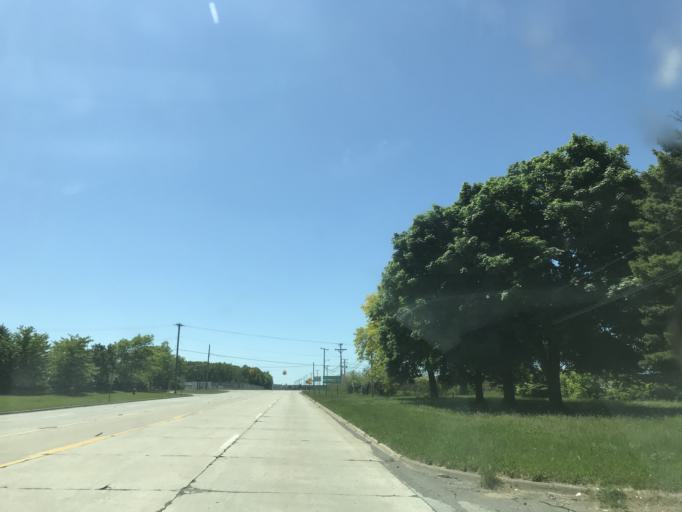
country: US
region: Michigan
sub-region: Wayne County
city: Taylor
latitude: 42.2100
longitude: -83.3244
